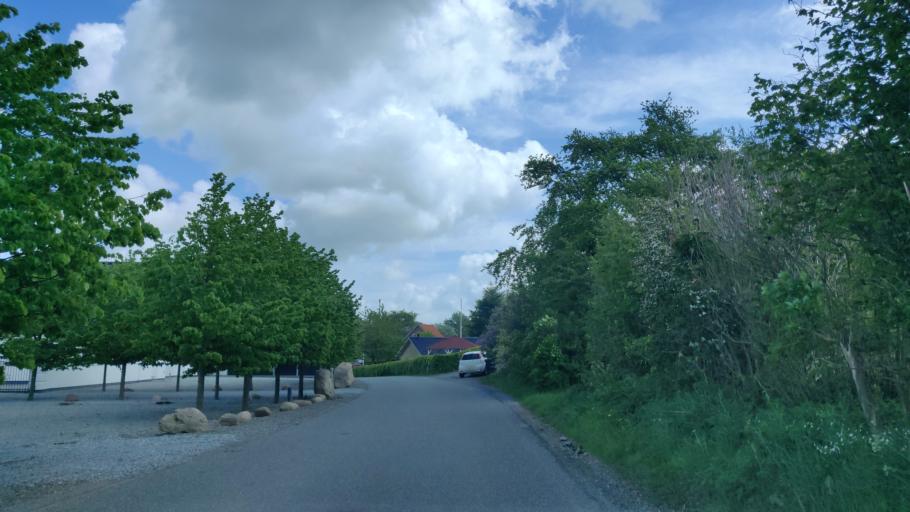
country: DK
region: South Denmark
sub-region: Vejle Kommune
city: Vejle
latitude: 55.6571
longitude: 9.5158
